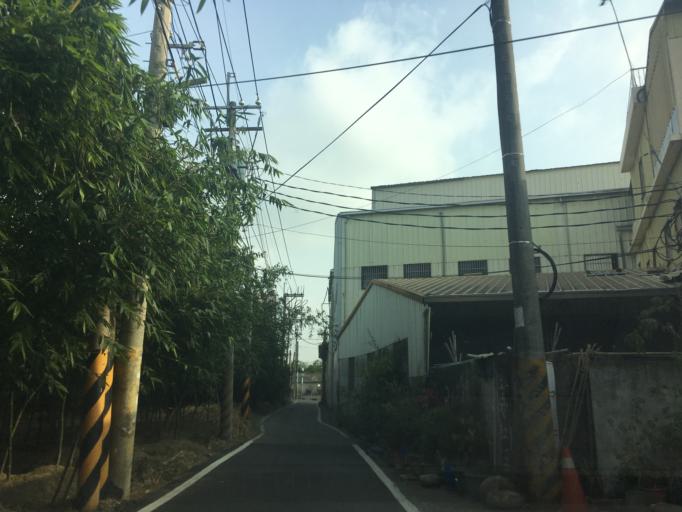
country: TW
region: Taiwan
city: Fengyuan
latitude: 24.2298
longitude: 120.7269
